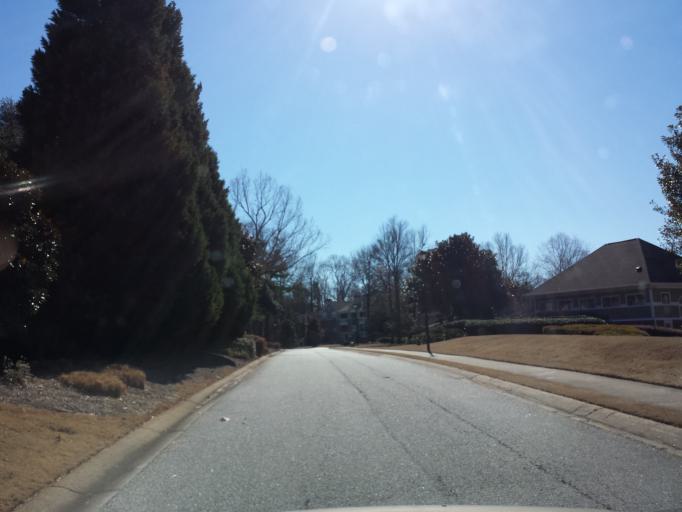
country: US
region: Georgia
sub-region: Cobb County
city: Vinings
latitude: 33.8997
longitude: -84.4544
